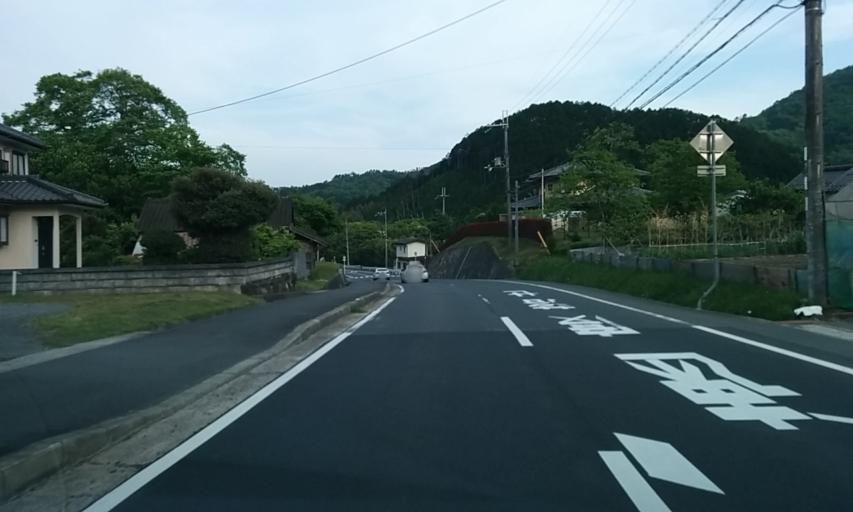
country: JP
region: Kyoto
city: Ayabe
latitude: 35.1614
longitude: 135.4089
